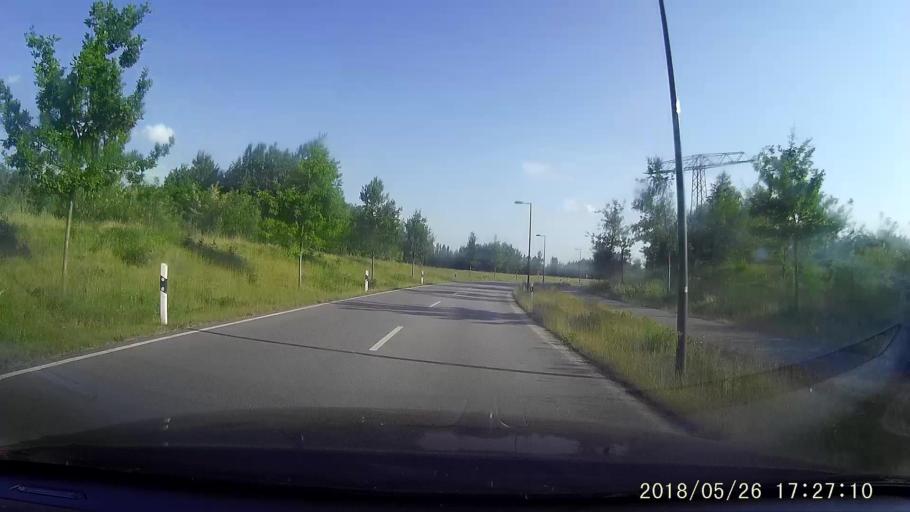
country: DE
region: Saxony
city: Ostritz
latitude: 51.0713
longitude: 14.9570
